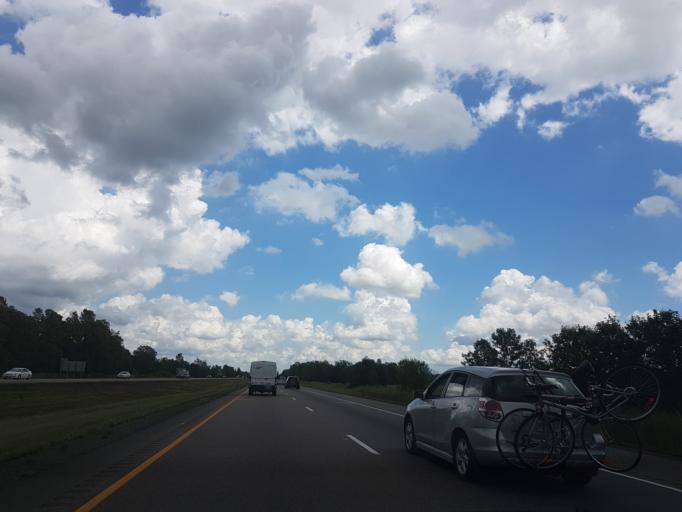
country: CA
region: Ontario
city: Deseronto
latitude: 44.2424
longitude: -77.0775
